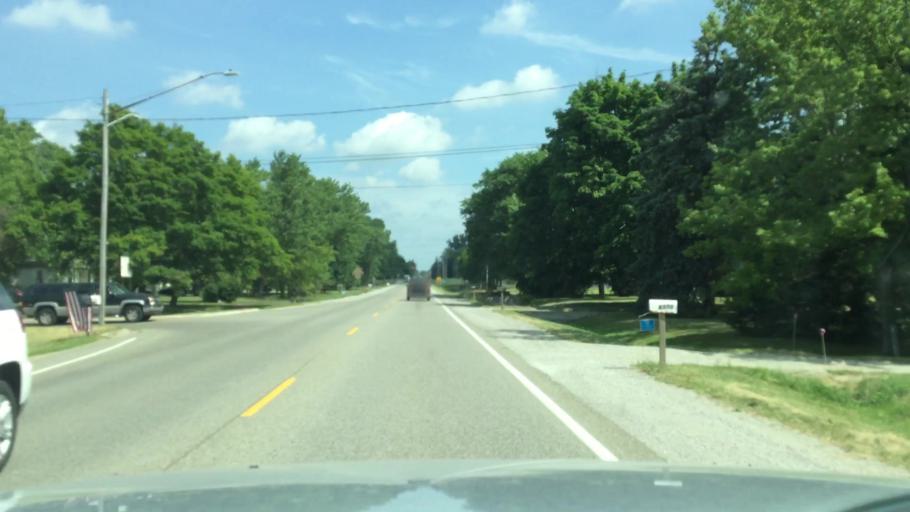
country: US
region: Michigan
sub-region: Genesee County
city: Flushing
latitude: 43.0634
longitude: -83.8132
